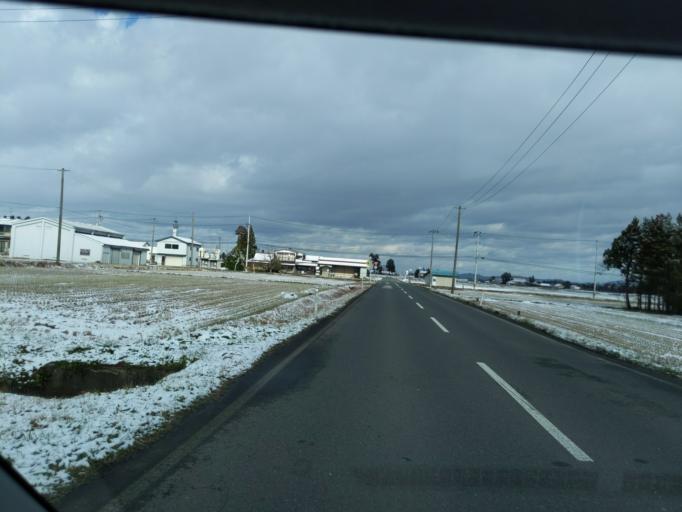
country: JP
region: Iwate
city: Mizusawa
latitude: 39.1534
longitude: 141.1134
